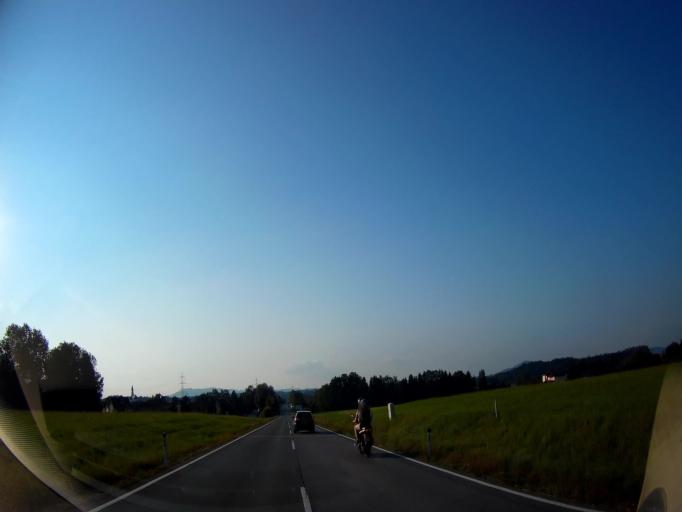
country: AT
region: Salzburg
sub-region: Politischer Bezirk Salzburg-Umgebung
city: Eugendorf
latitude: 47.8639
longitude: 13.1364
